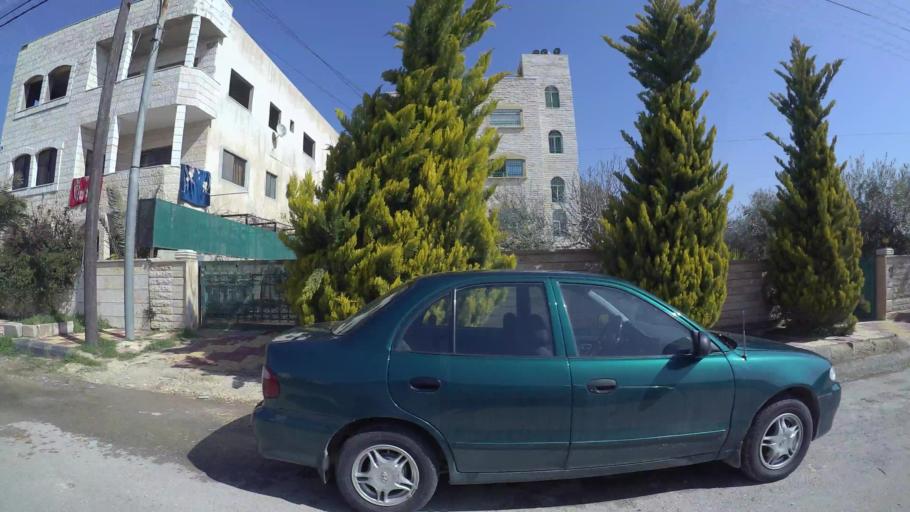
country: JO
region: Amman
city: Al Bunayyat ash Shamaliyah
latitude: 31.8980
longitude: 35.8968
